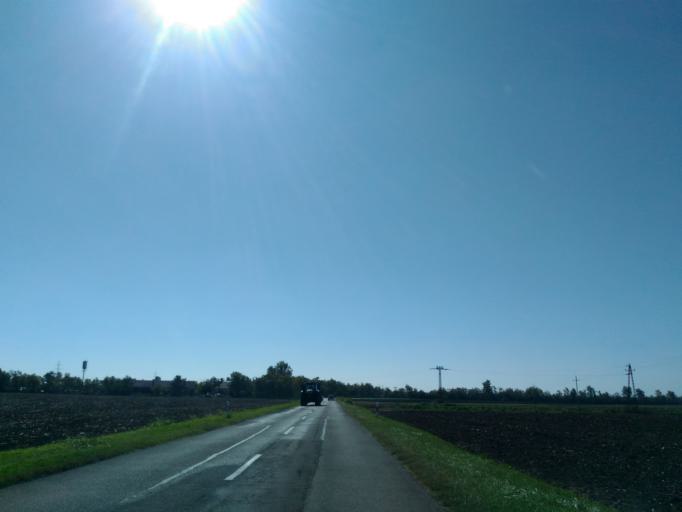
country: HU
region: Fejer
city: Ivancsa
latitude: 47.1712
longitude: 18.7946
